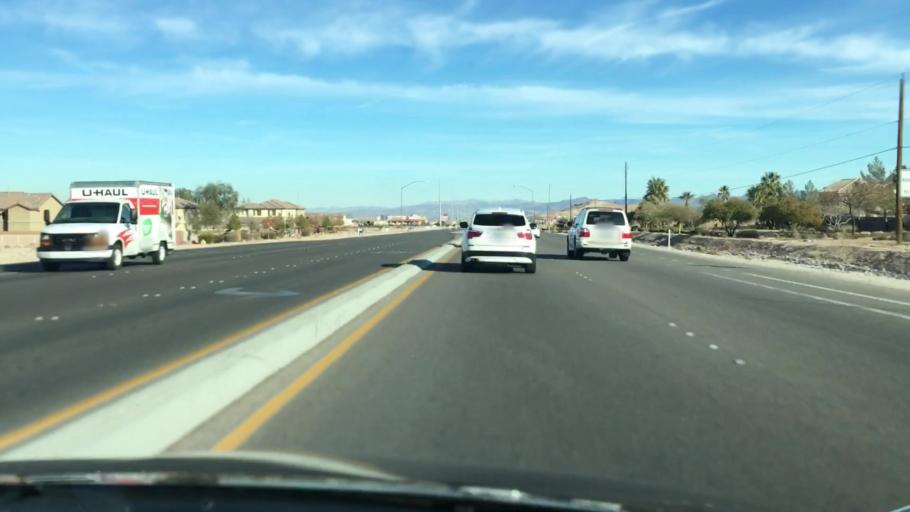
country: US
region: Nevada
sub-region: Clark County
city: Enterprise
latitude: 36.0201
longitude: -115.2873
